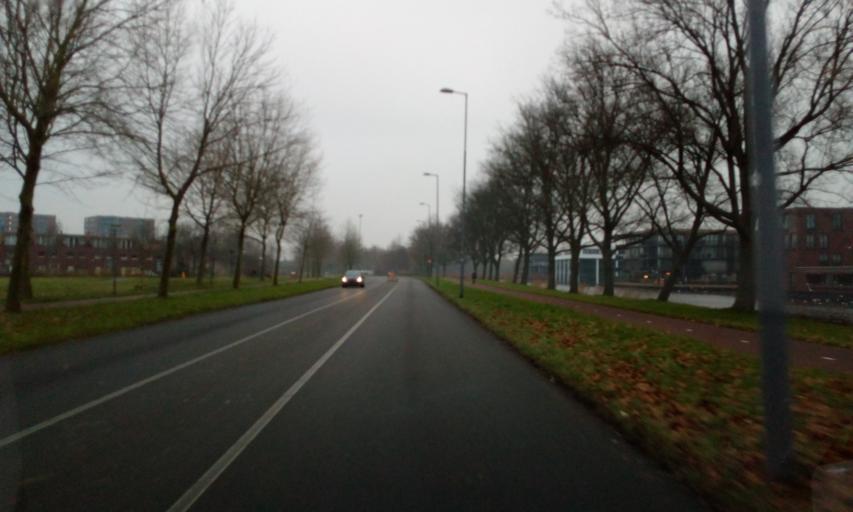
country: NL
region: South Holland
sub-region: Gemeente Lansingerland
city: Bergschenhoek
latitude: 51.9650
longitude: 4.4930
